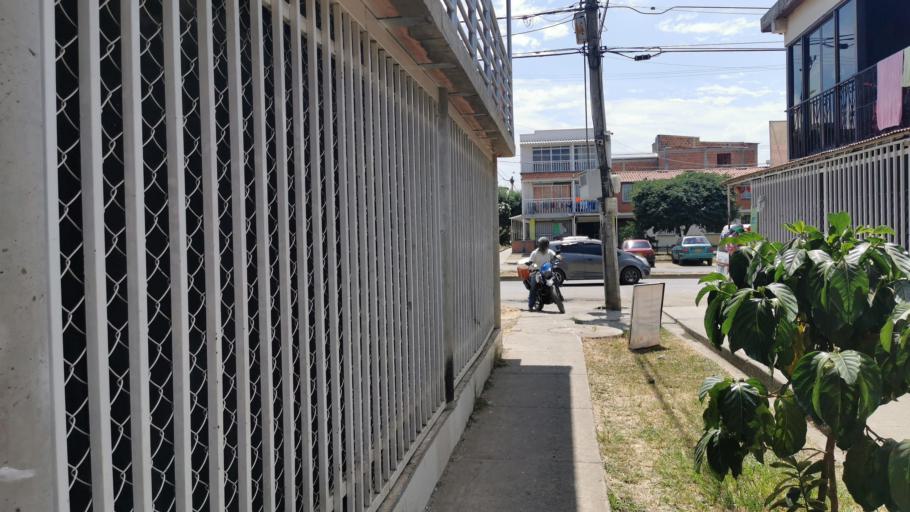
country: CO
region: Valle del Cauca
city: Jamundi
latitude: 3.2413
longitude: -76.5161
